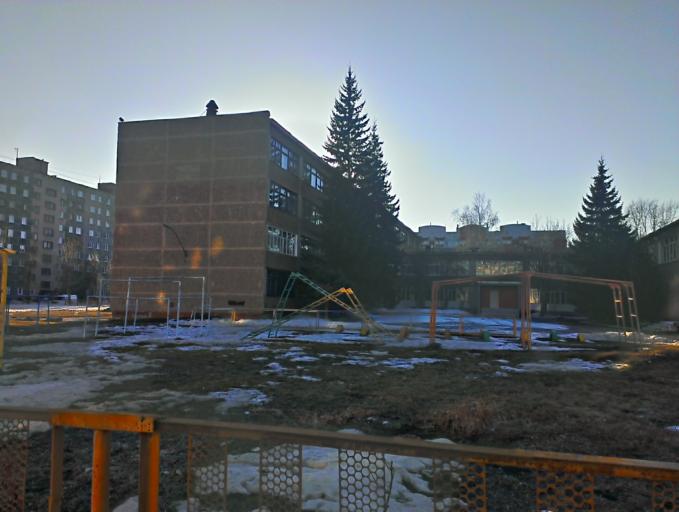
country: RU
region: Altai Krai
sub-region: Gorod Barnaulskiy
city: Barnaul
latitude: 53.3626
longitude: 83.6849
